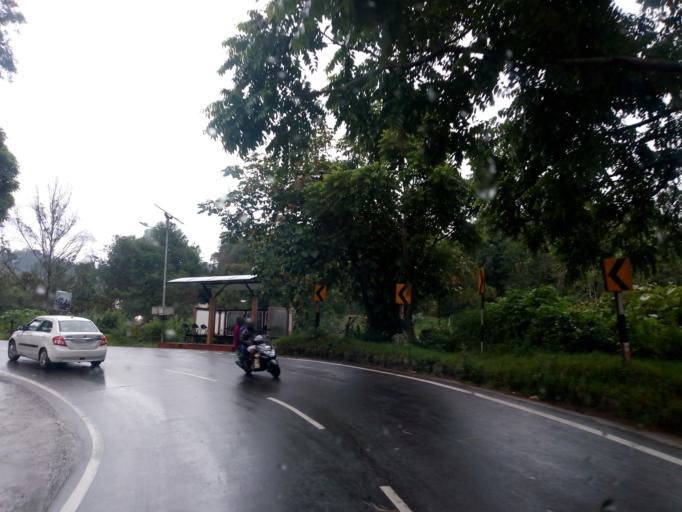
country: IN
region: Tamil Nadu
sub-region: Nilgiri
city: Wellington
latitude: 11.3591
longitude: 76.7839
